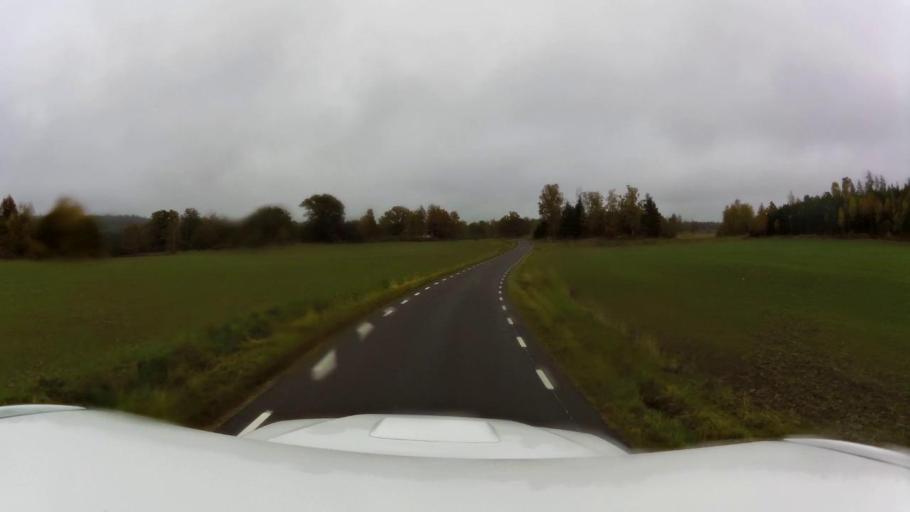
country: SE
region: OEstergoetland
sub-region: Linkopings Kommun
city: Linghem
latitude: 58.3525
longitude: 15.8733
